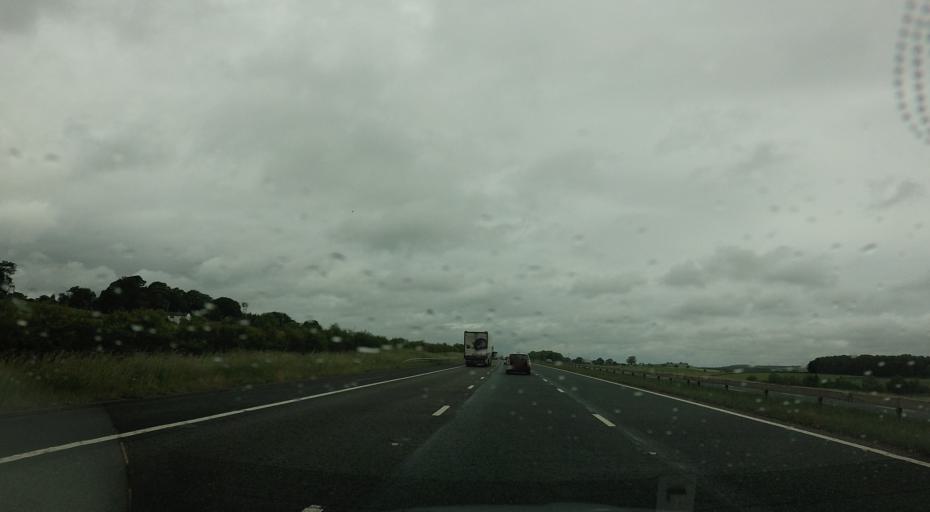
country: GB
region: England
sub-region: Cumbria
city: Penrith
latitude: 54.7354
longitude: -2.8053
